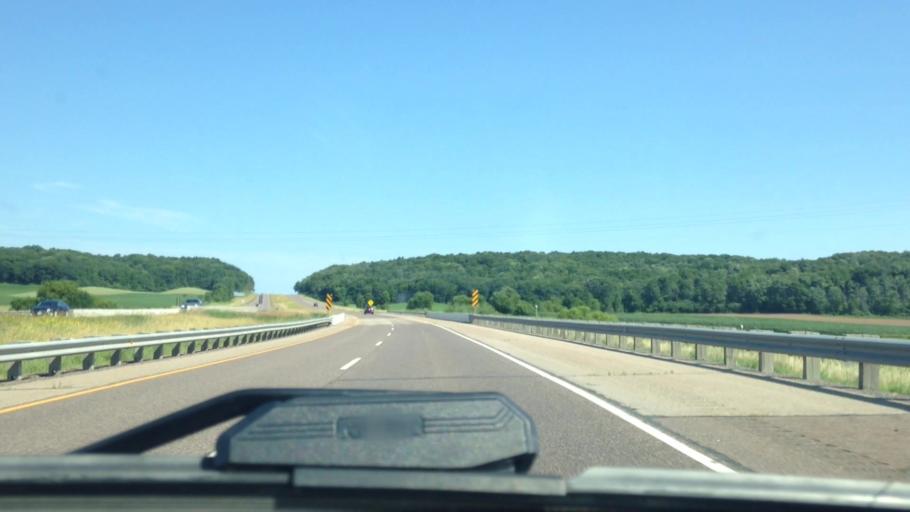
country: US
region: Wisconsin
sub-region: Chippewa County
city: Chippewa Falls
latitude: 44.9650
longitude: -91.4264
